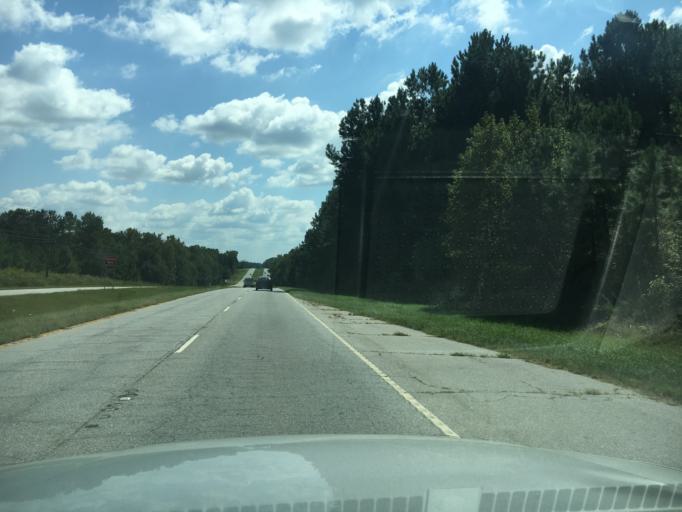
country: US
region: South Carolina
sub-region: Greenwood County
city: Greenwood
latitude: 34.2706
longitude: -82.2310
